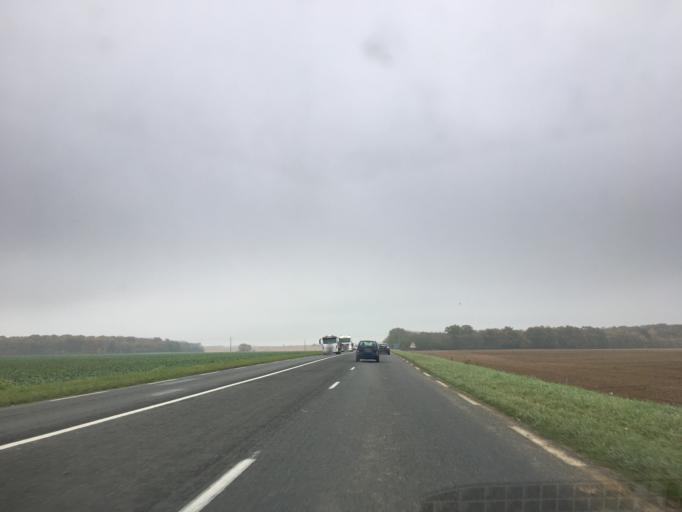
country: FR
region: Ile-de-France
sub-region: Departement de Seine-et-Marne
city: Cannes-Ecluse
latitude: 48.3547
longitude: 2.9965
